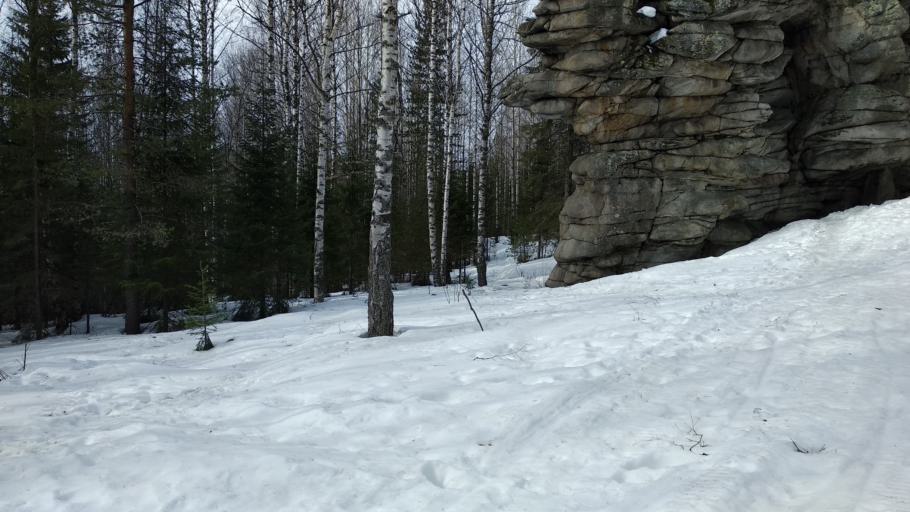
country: RU
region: Sverdlovsk
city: Karpinsk
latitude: 59.5703
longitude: 59.3437
